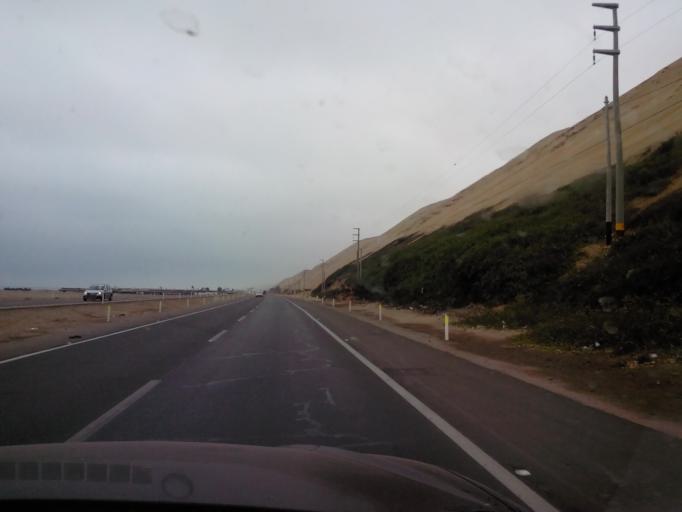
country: PE
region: Ica
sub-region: Provincia de Chincha
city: San Pedro
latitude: -13.3455
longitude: -76.2269
